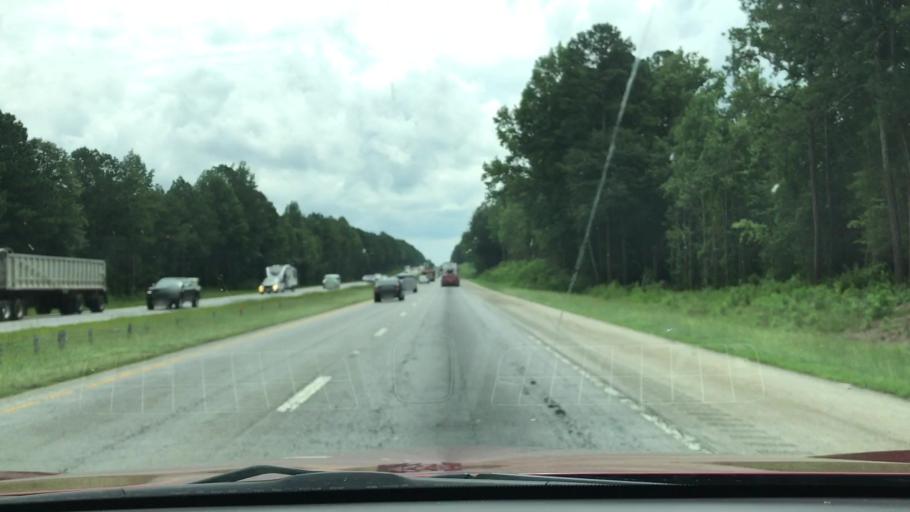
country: US
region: South Carolina
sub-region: Laurens County
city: Joanna
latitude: 34.4349
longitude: -81.7504
